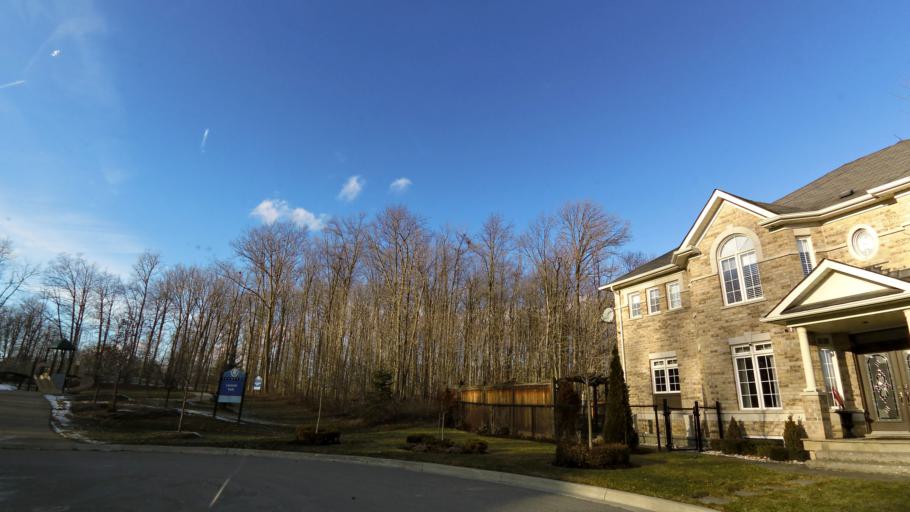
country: CA
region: Ontario
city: Brampton
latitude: 43.6360
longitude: -79.7745
